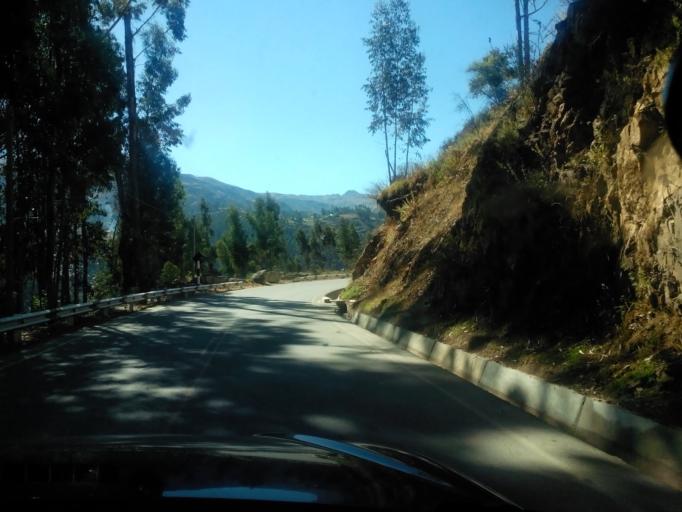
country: PE
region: Apurimac
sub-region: Provincia de Andahuaylas
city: Talavera
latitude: -13.6553
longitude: -73.4854
